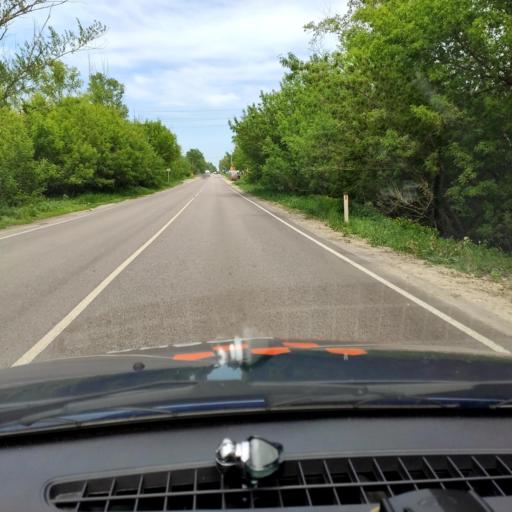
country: RU
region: Voronezj
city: Maslovka
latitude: 51.5312
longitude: 39.3123
